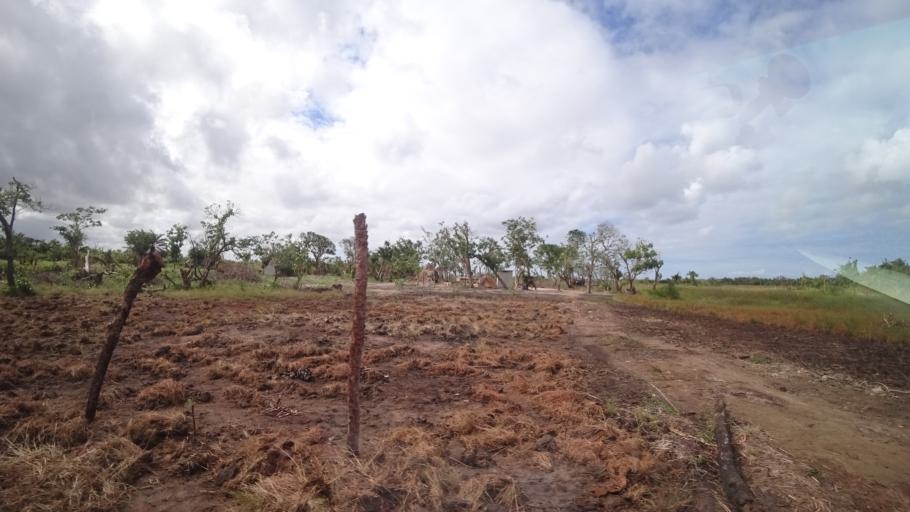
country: MZ
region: Sofala
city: Beira
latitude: -19.6113
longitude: 35.2155
